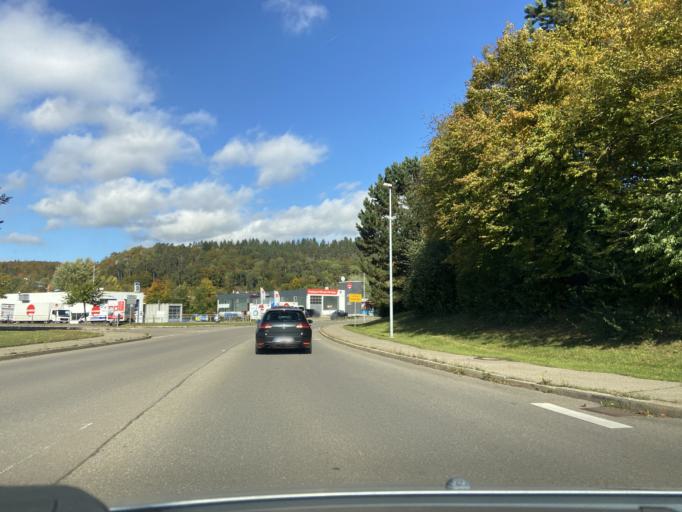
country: DE
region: Baden-Wuerttemberg
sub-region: Tuebingen Region
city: Sigmaringen
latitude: 48.0871
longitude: 9.2079
